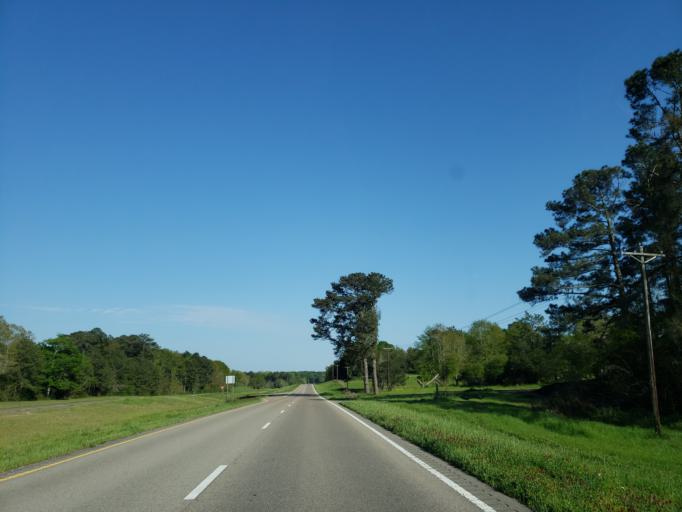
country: US
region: Mississippi
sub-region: Jones County
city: Ellisville
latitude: 31.6869
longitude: -89.3230
